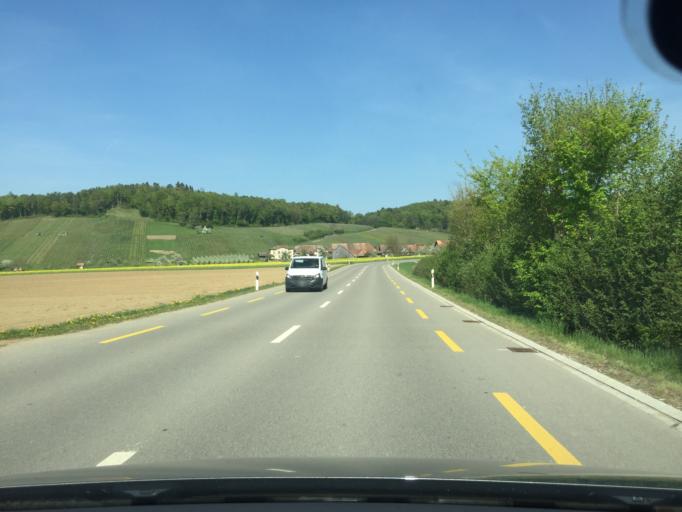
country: CH
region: Zurich
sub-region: Bezirk Andelfingen
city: Marthalen
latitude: 47.6380
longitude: 8.6668
